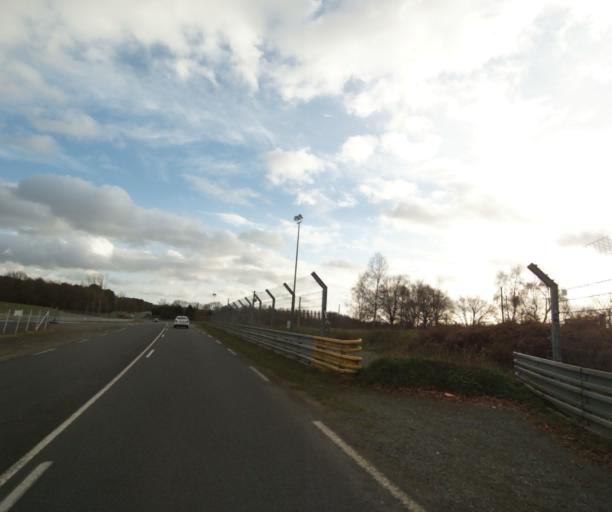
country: FR
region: Pays de la Loire
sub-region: Departement de la Sarthe
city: Arnage
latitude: 47.9331
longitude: 0.2085
